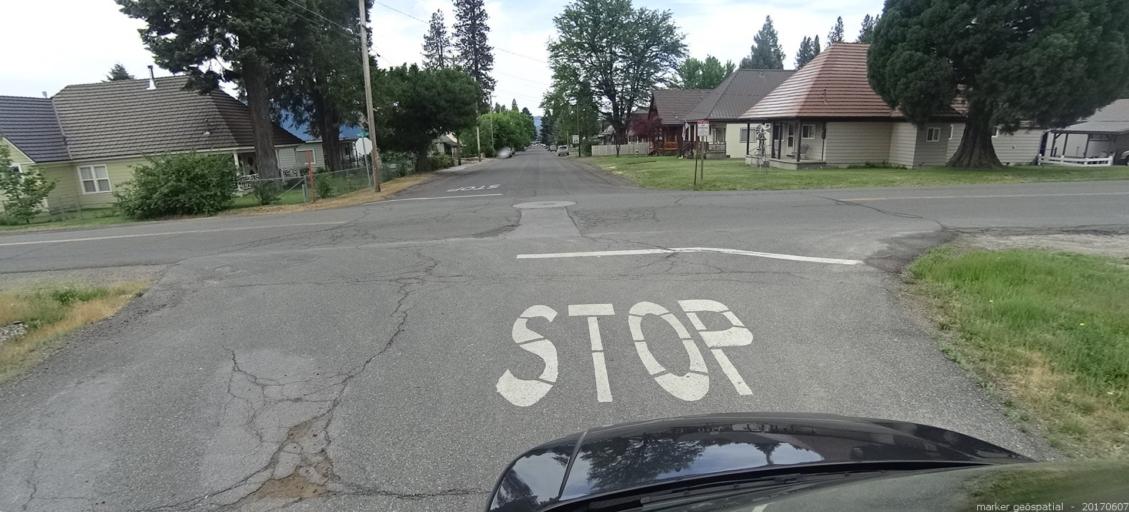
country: US
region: California
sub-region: Siskiyou County
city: McCloud
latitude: 41.2586
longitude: -122.1381
